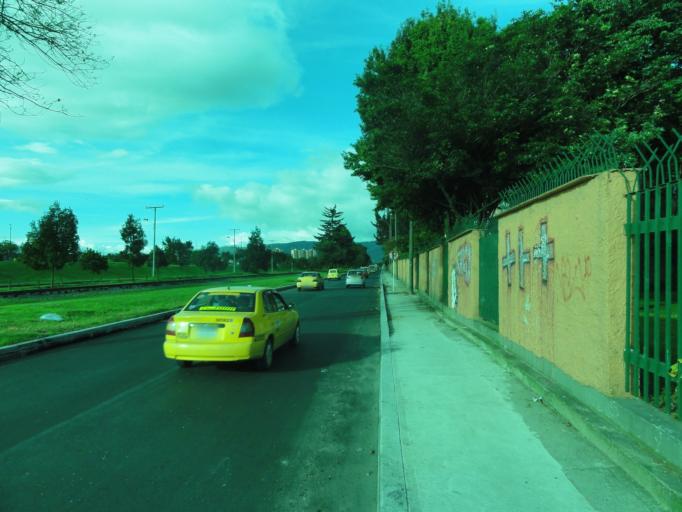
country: CO
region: Bogota D.C.
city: Bogota
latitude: 4.6532
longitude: -74.0910
